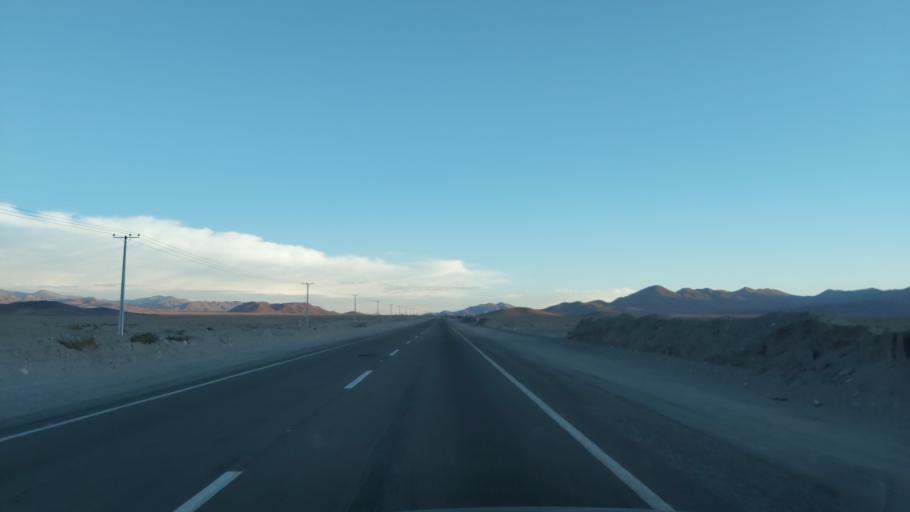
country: CL
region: Atacama
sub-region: Provincia de Chanaral
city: Diego de Almagro
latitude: -26.7077
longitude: -69.9235
